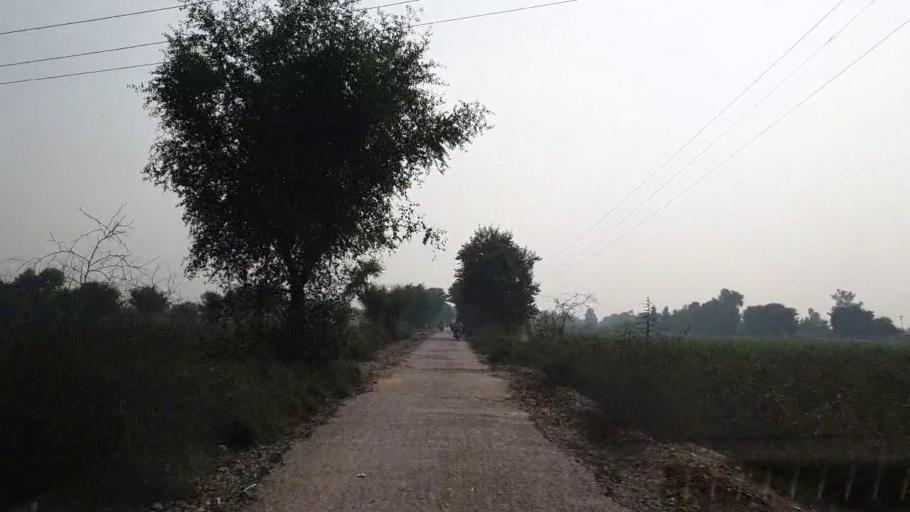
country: PK
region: Sindh
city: Bhan
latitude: 26.5842
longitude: 67.7306
